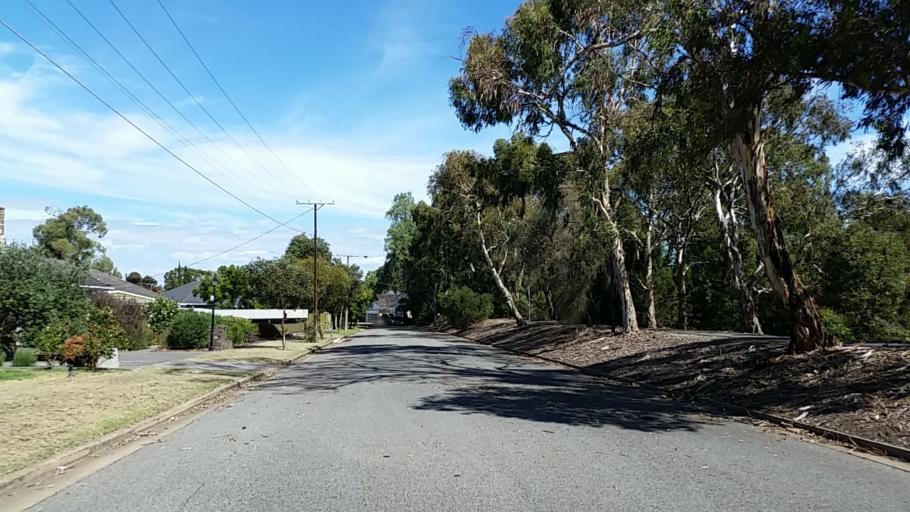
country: AU
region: South Australia
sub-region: Charles Sturt
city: Seaton
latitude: -34.9217
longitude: 138.5210
